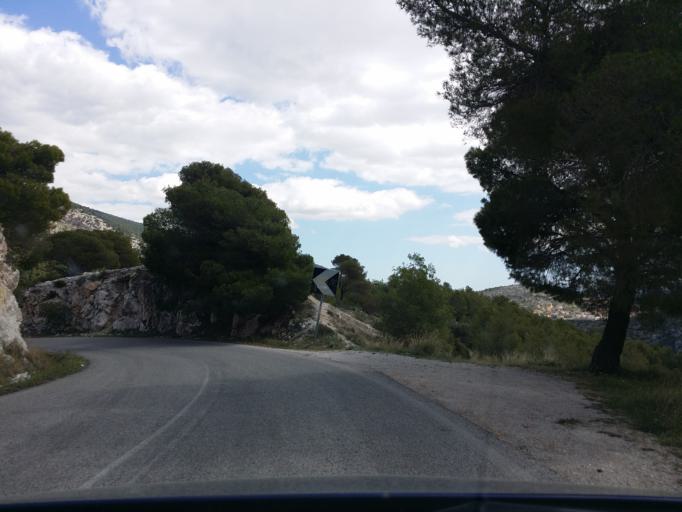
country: GR
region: Attica
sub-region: Nomarchia Dytikis Attikis
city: Fyli
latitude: 38.1181
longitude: 23.6532
